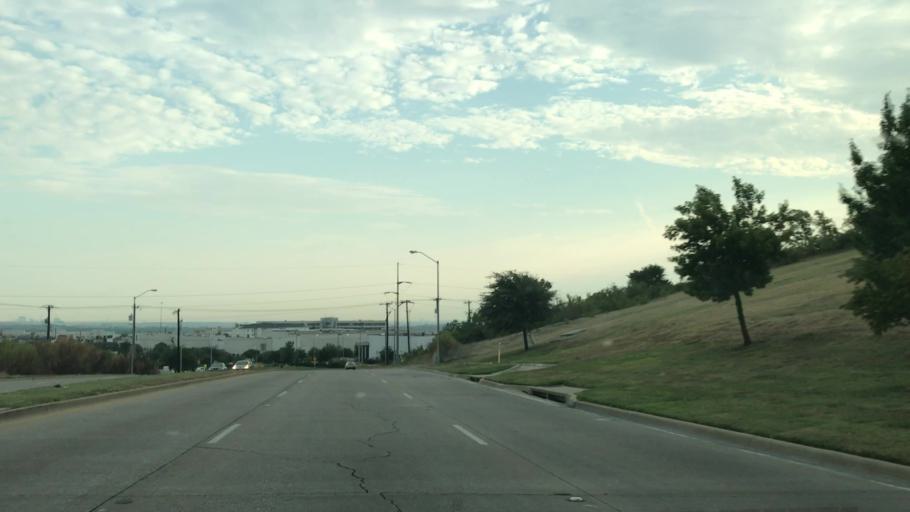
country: US
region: Texas
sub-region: Dallas County
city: Cockrell Hill
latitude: 32.7574
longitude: -96.8929
